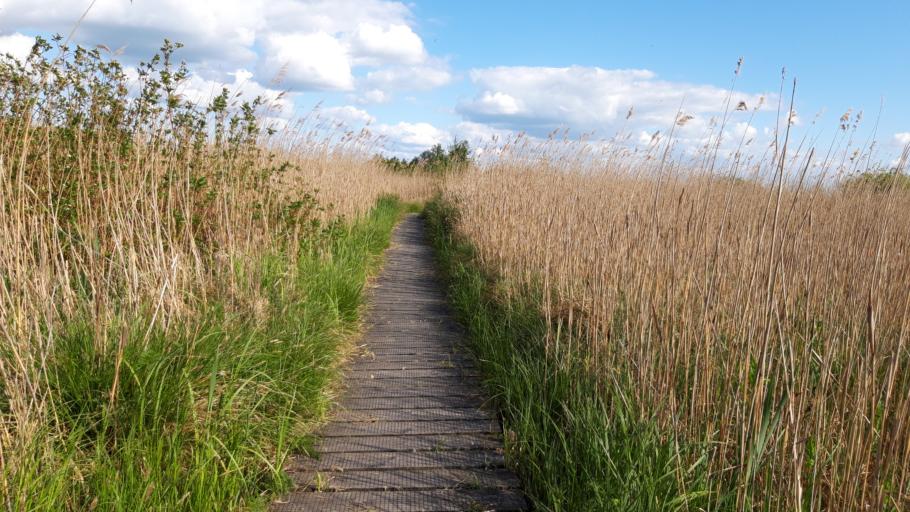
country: NL
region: Utrecht
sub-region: Gemeente Lopik
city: Lopik
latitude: 51.9552
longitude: 4.9899
